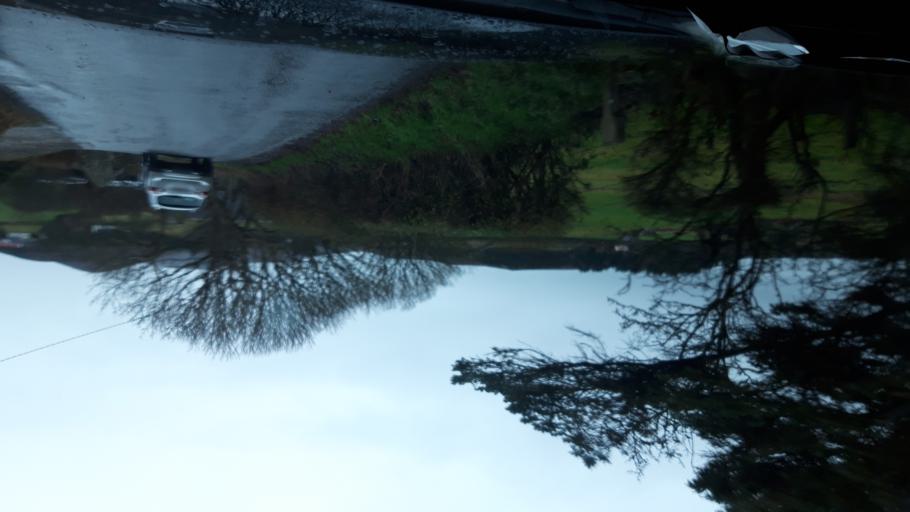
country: IE
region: Ulster
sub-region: County Donegal
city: Buncrana
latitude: 55.2510
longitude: -7.6270
